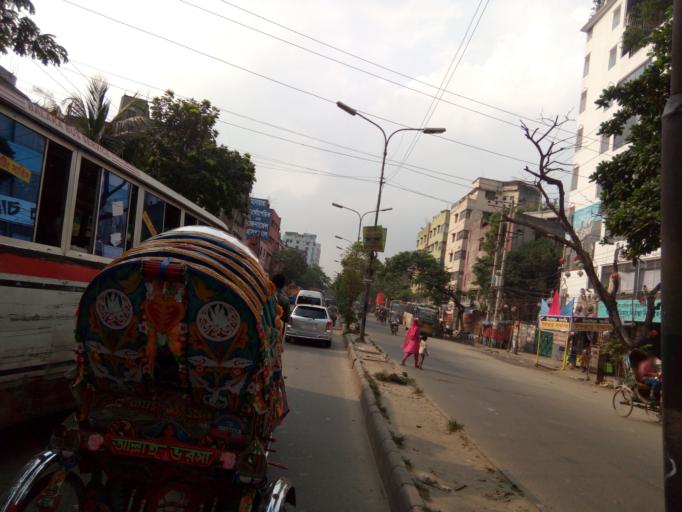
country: BD
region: Dhaka
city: Paltan
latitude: 23.7188
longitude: 90.4290
